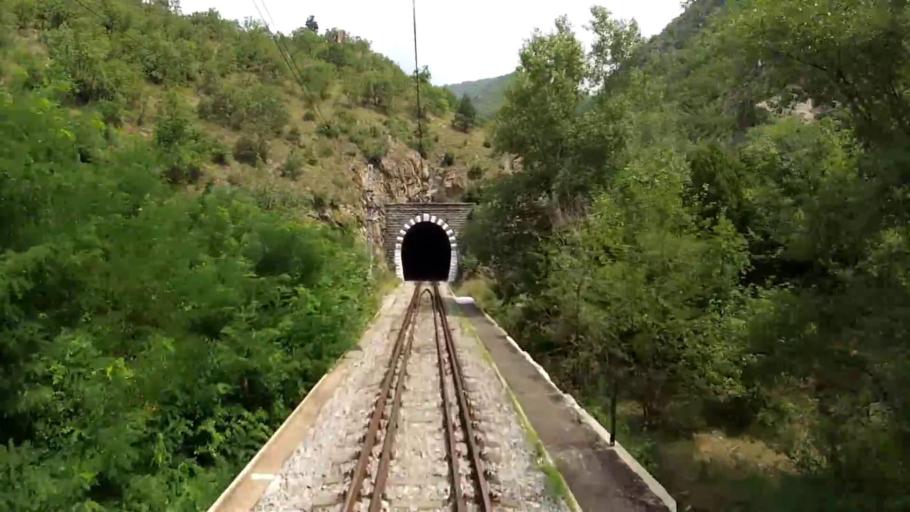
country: BG
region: Blagoevgrad
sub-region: Obshtina Kresna
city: Stara Kresna
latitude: 41.8243
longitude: 23.1587
